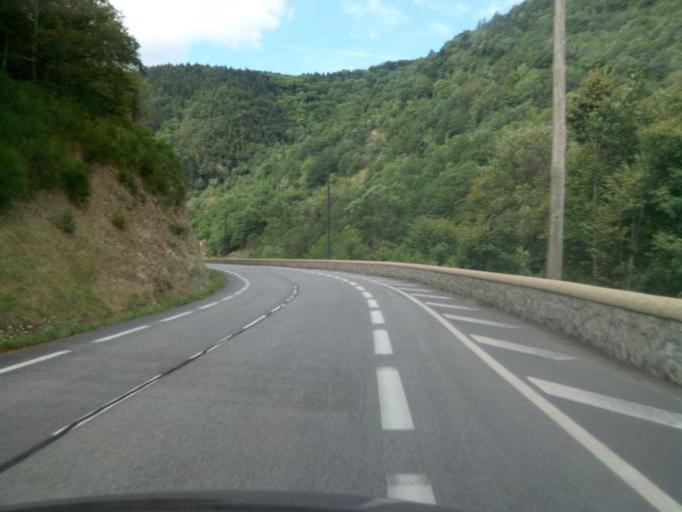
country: FR
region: Auvergne
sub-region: Departement de la Haute-Loire
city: Chadrac
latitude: 45.1102
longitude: 3.8923
